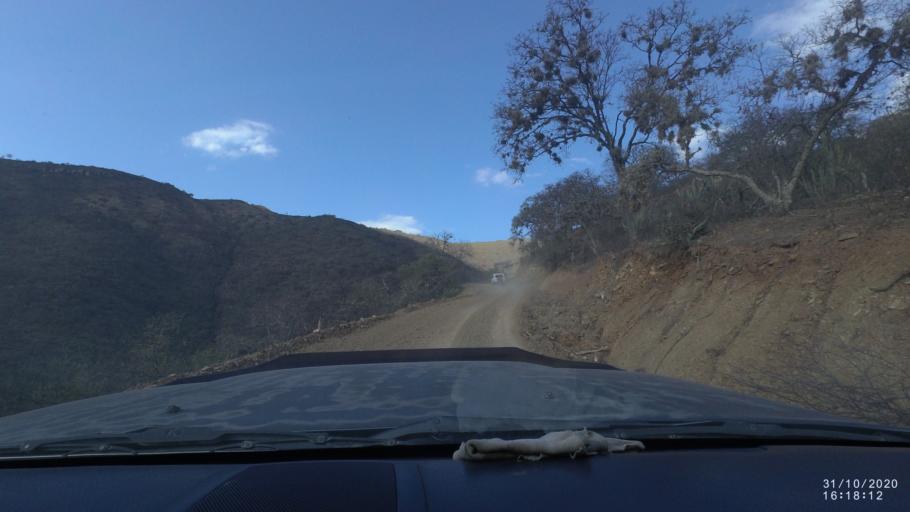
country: BO
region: Chuquisaca
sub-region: Provincia Zudanez
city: Mojocoya
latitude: -18.3919
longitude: -64.6040
